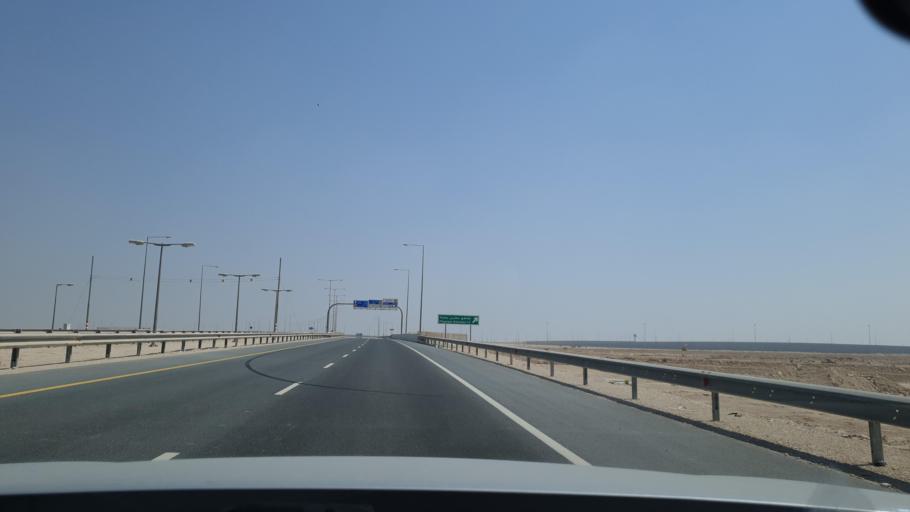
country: QA
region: Baladiyat az Za`ayin
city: Az Za`ayin
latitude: 25.6181
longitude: 51.3569
